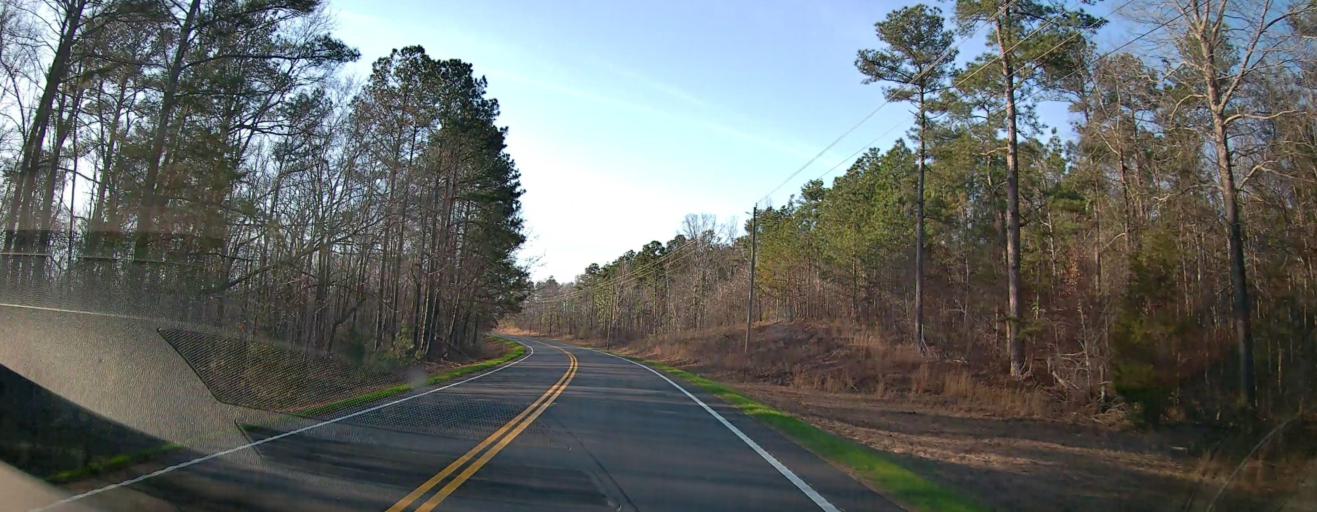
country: US
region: Georgia
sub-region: Harris County
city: Hamilton
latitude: 32.7455
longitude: -84.9796
